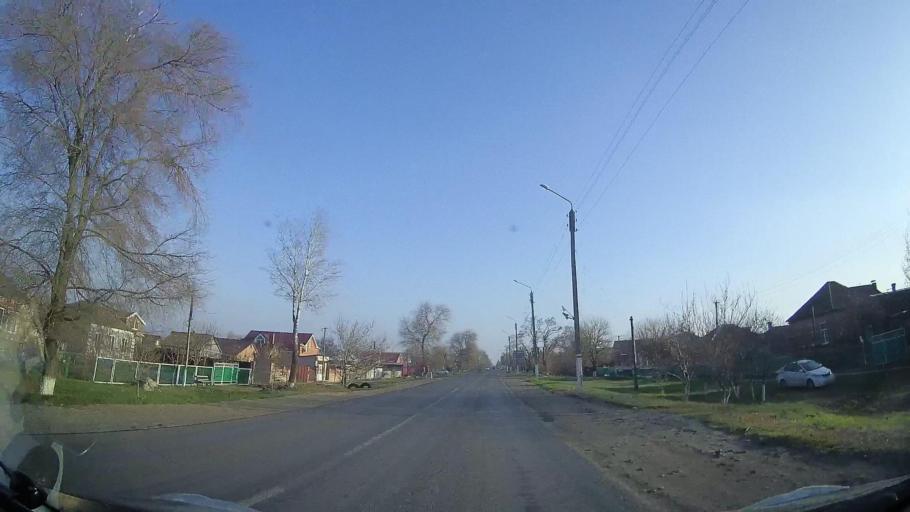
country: RU
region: Rostov
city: Ol'ginskaya
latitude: 47.1978
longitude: 39.9374
